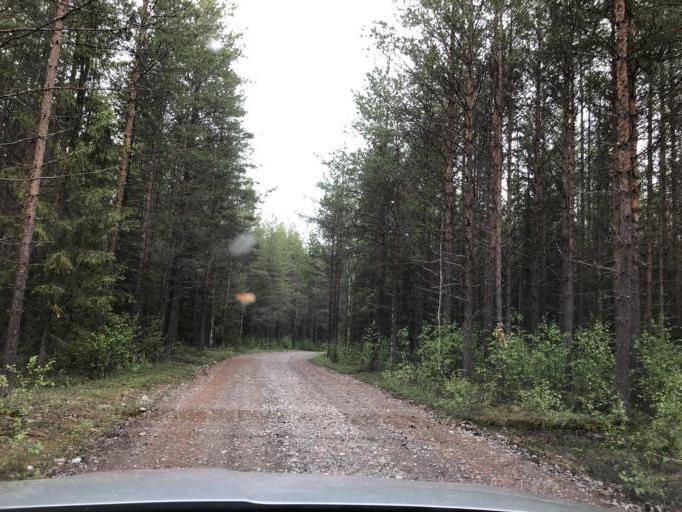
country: SE
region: Norrbotten
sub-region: Pitea Kommun
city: Roknas
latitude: 65.4076
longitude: 21.2602
